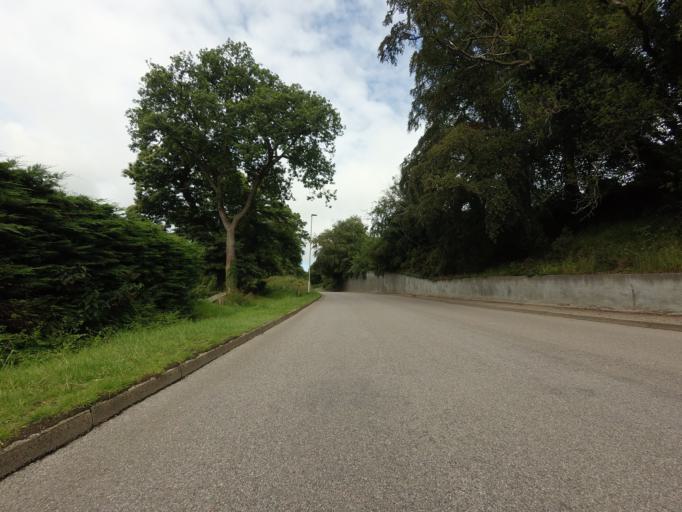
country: GB
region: Scotland
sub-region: Moray
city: Elgin
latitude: 57.6528
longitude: -3.3394
